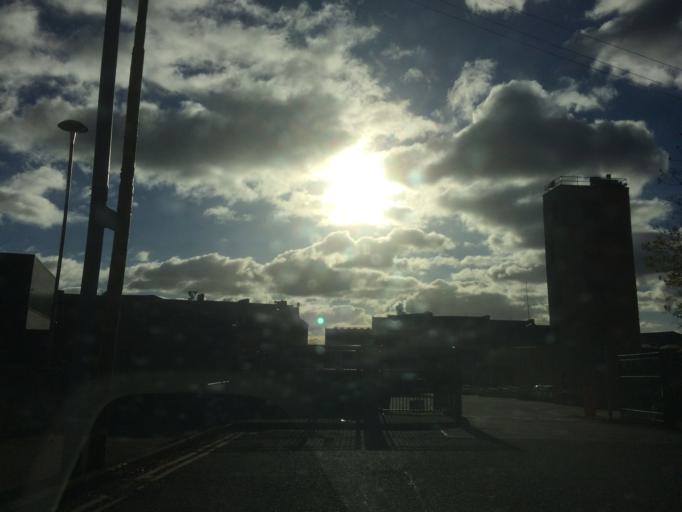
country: GB
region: Scotland
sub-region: Glasgow City
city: Glasgow
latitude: 55.8565
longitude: -4.2345
